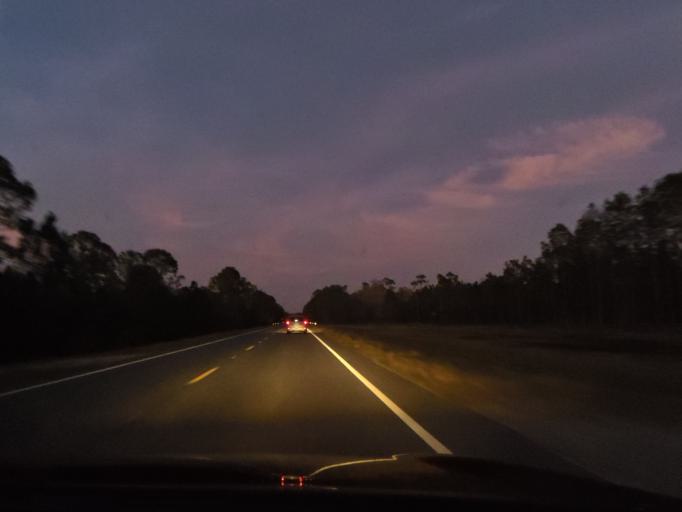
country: US
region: Florida
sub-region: Volusia County
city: De Leon Springs
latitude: 29.2425
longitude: -81.2282
